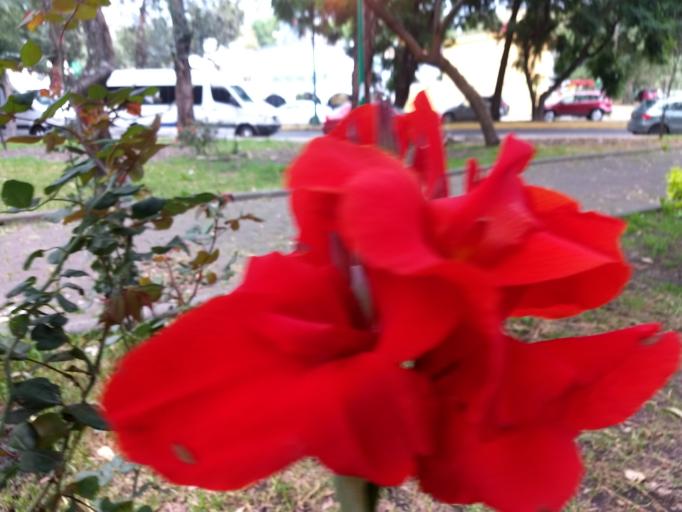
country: MX
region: Mexico City
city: Tlalpan
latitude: 19.3068
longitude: -99.1234
